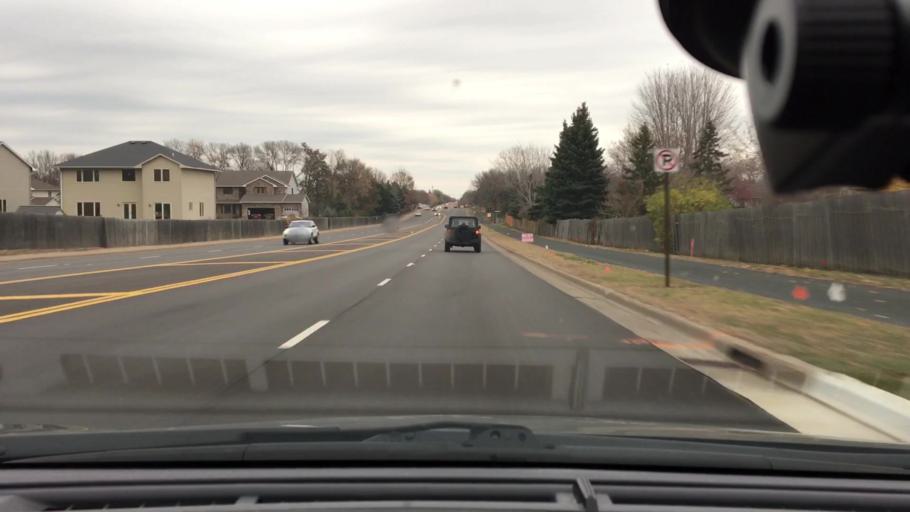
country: US
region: Minnesota
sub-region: Hennepin County
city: Maple Grove
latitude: 45.1234
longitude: -93.4724
